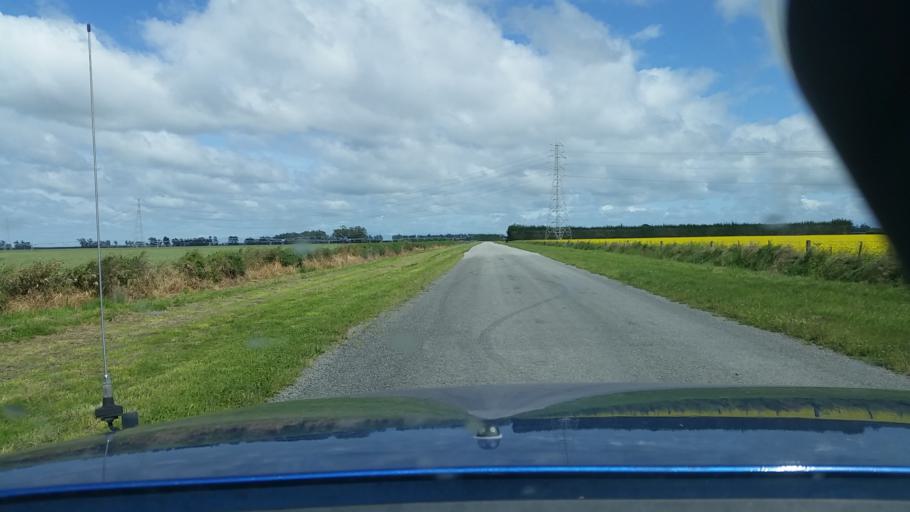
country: NZ
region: Canterbury
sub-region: Ashburton District
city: Rakaia
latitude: -43.8362
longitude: 171.9802
